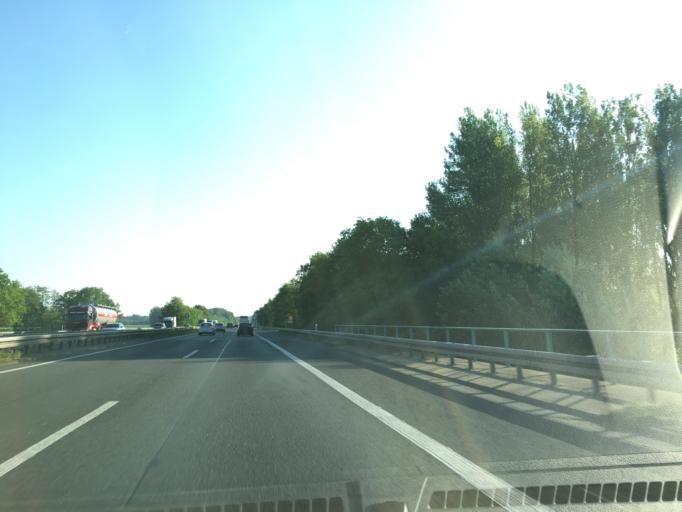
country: DE
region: North Rhine-Westphalia
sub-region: Regierungsbezirk Munster
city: Greven
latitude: 52.0514
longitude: 7.6148
